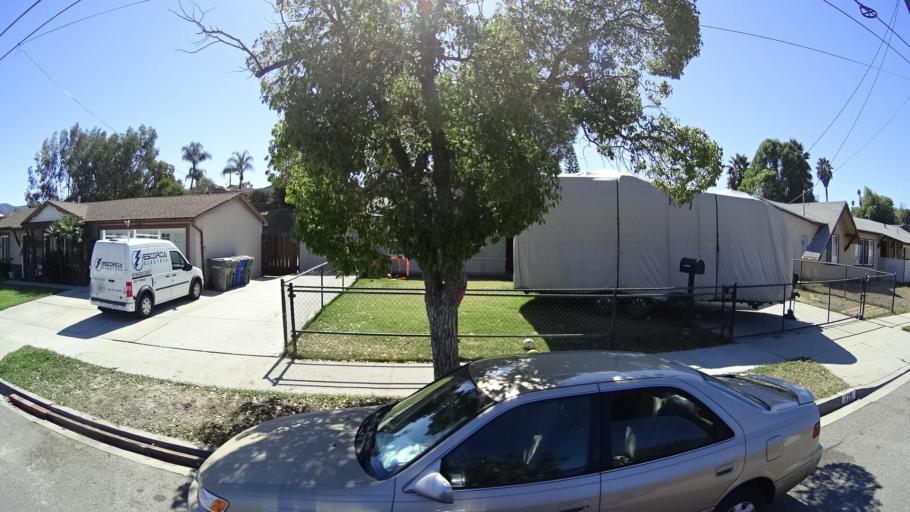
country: US
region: California
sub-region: San Diego County
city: La Presa
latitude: 32.7025
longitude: -117.0158
